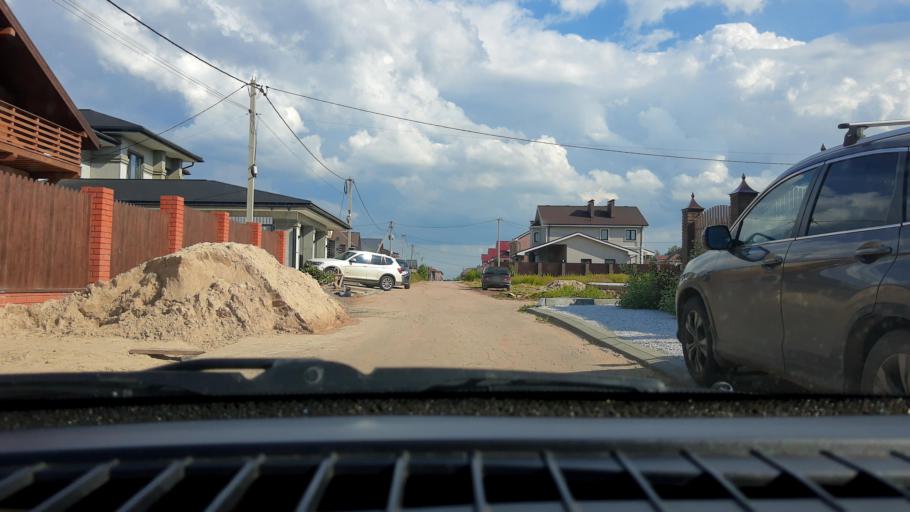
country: RU
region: Nizjnij Novgorod
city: Afonino
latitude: 56.2508
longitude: 44.0338
